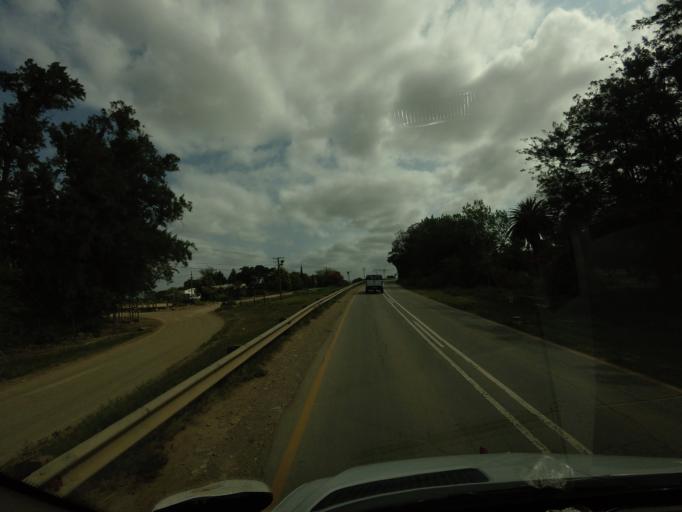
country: ZA
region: Eastern Cape
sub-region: Cacadu District Municipality
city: Kirkwood
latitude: -33.5066
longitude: 25.6933
